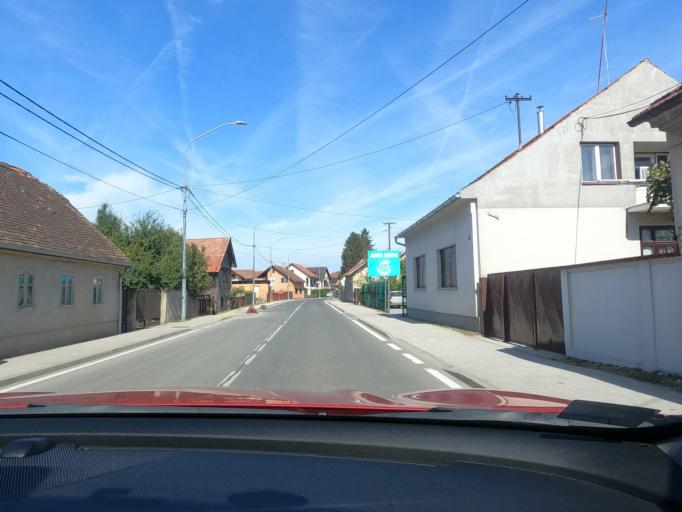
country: HR
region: Sisacko-Moslavacka
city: Petrinja
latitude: 45.4300
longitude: 16.2793
